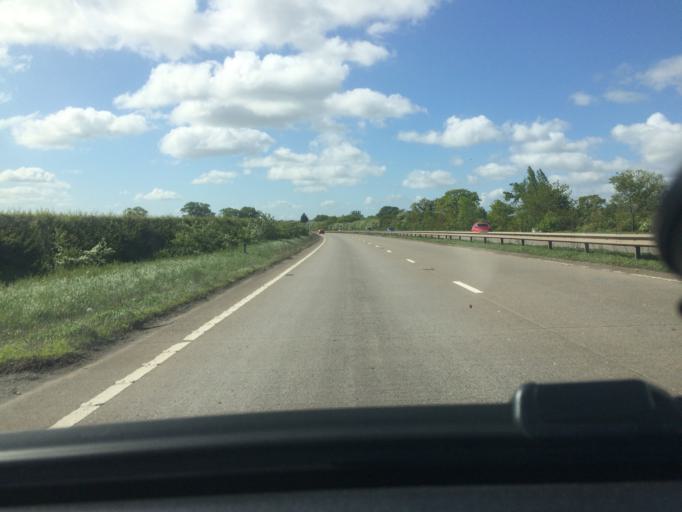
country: GB
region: Wales
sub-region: Wrexham
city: Rossett
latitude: 53.1371
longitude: -2.9448
